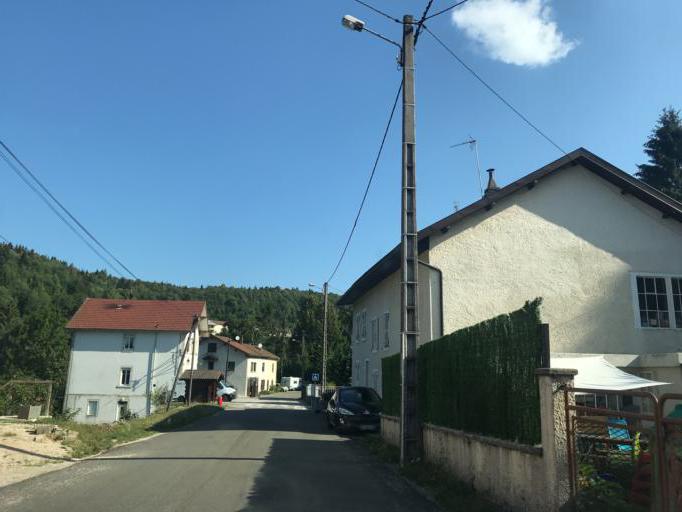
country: FR
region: Franche-Comte
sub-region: Departement du Jura
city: Moirans-en-Montagne
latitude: 46.4147
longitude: 5.7350
